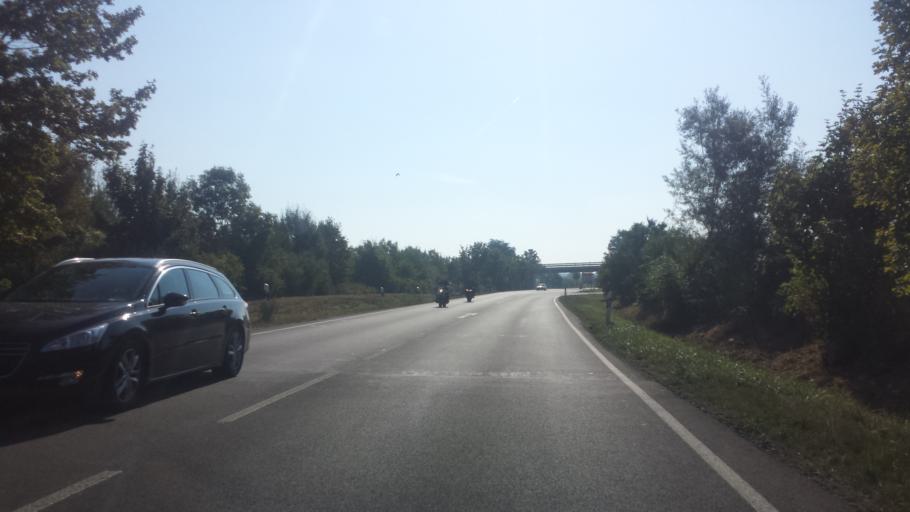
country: DE
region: Rheinland-Pfalz
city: Heidesheim
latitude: 49.5663
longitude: 8.1876
